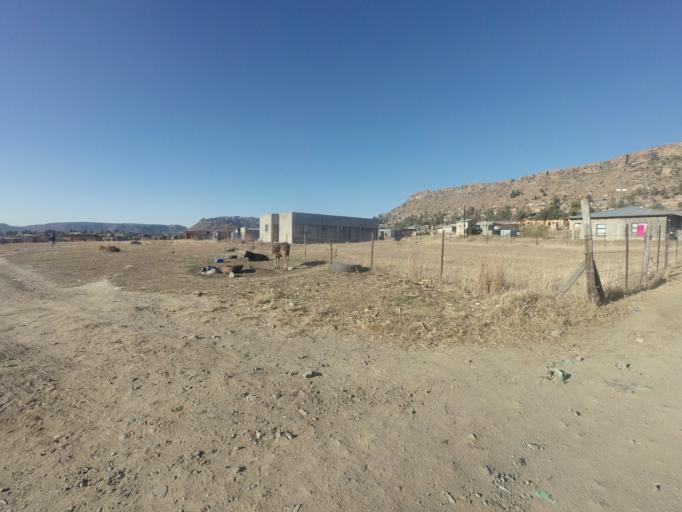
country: LS
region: Maseru
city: Maseru
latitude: -29.3009
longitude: 27.5470
